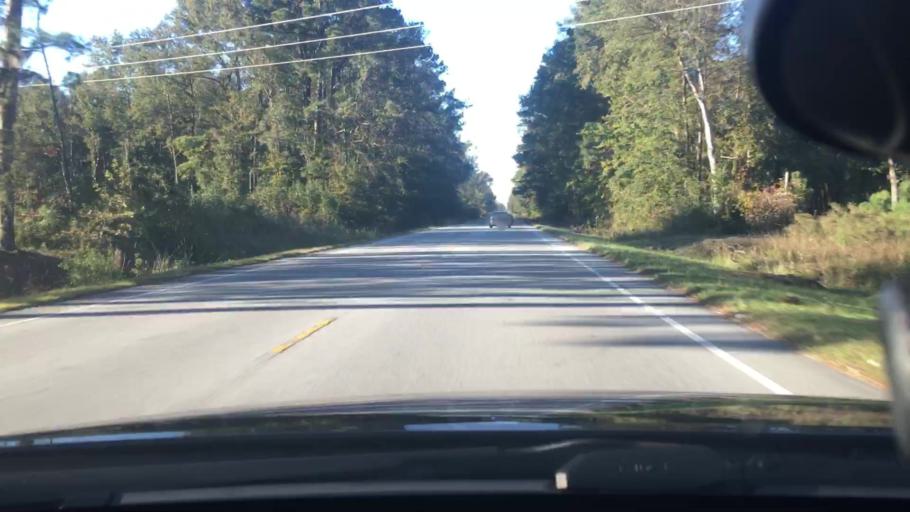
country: US
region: North Carolina
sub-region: Craven County
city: New Bern
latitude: 35.1633
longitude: -77.0396
